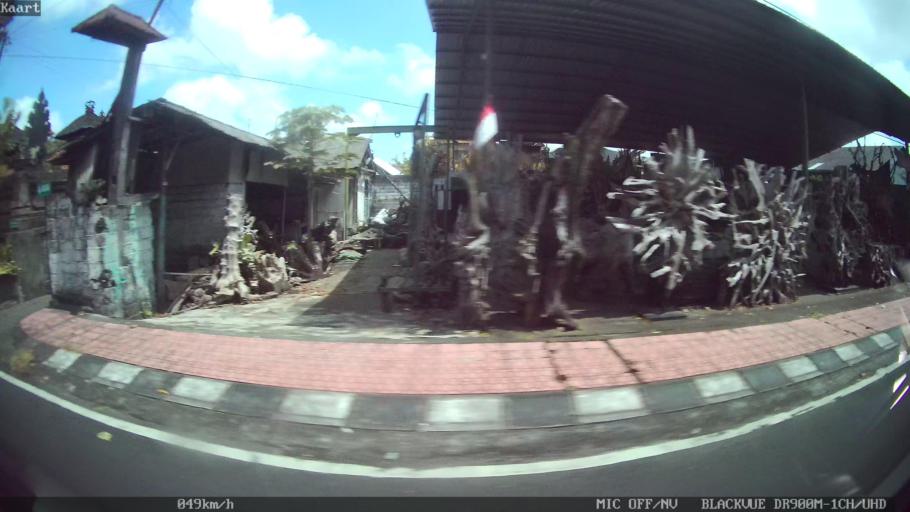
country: ID
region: Bali
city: Banjar Desa
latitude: -8.5841
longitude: 115.2822
